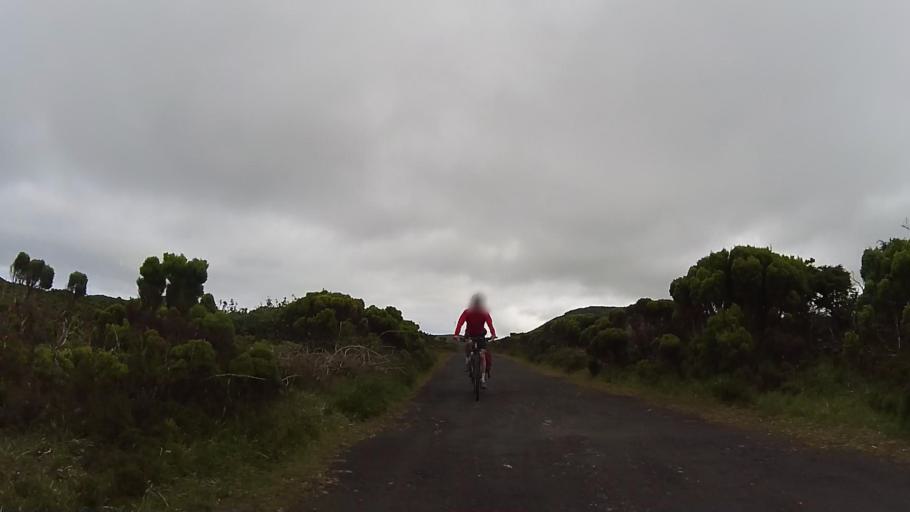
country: PT
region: Azores
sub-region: Sao Roque do Pico
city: Sao Roque do Pico
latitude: 38.4638
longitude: -28.2831
